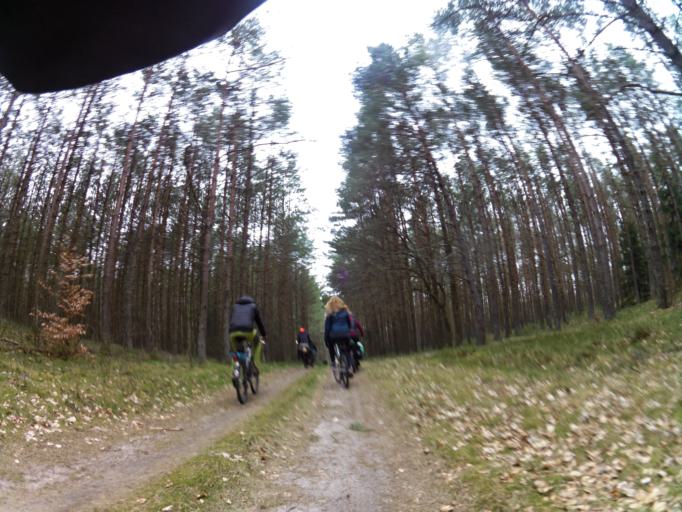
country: PL
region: West Pomeranian Voivodeship
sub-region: Powiat szczecinecki
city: Bialy Bor
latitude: 53.9359
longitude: 16.7427
